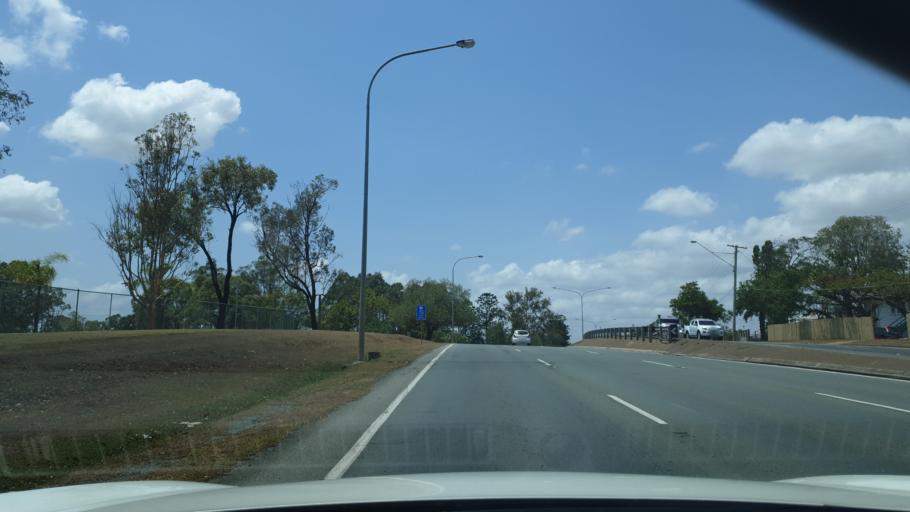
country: AU
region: Queensland
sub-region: Brisbane
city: Chermside West
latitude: -27.3758
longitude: 153.0268
